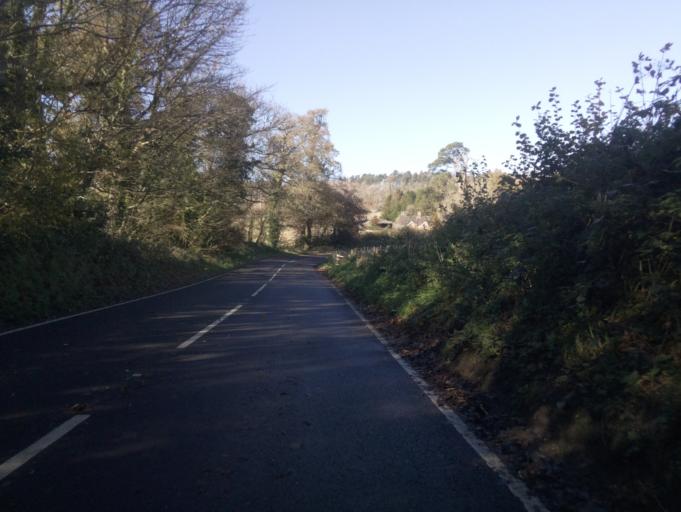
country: GB
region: England
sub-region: Dorset
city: Sherborne
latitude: 50.8419
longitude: -2.4902
